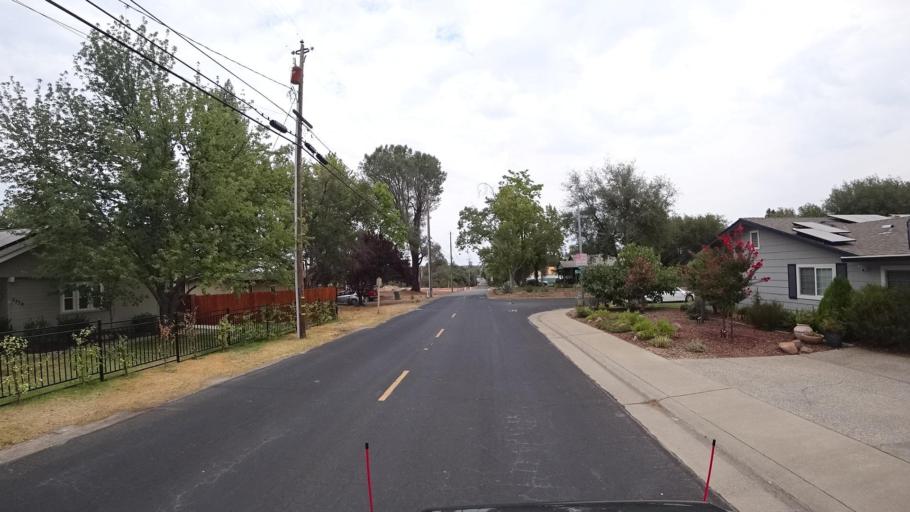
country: US
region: California
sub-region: Placer County
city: Rocklin
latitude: 38.7816
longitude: -121.2197
